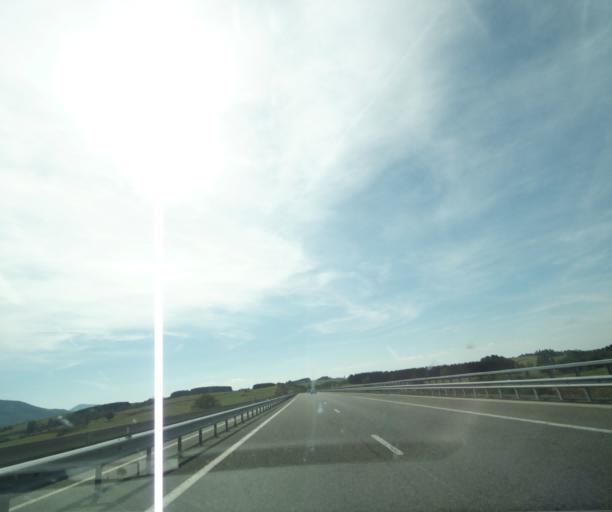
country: FR
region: Auvergne
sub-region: Departement du Puy-de-Dome
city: Saint-Ours
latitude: 45.8948
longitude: 2.9349
